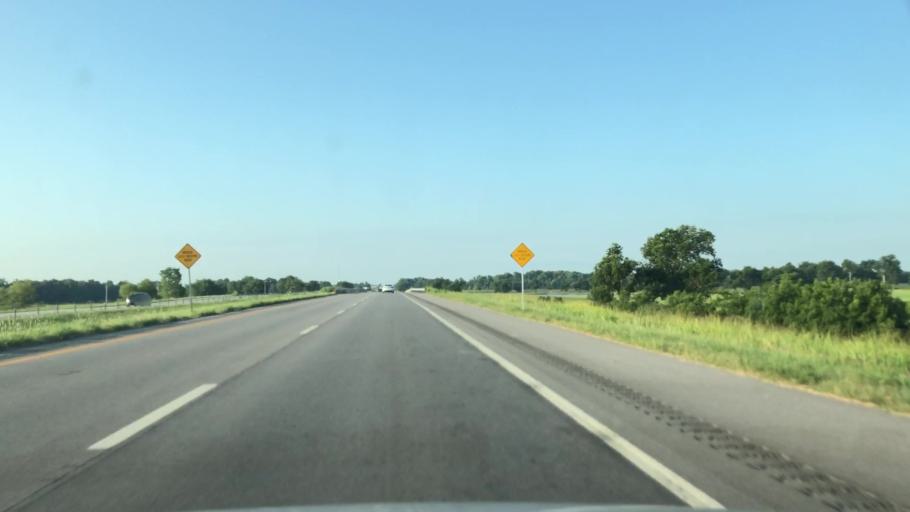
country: US
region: Oklahoma
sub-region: Washington County
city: Bartlesville
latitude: 36.6577
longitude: -95.9355
